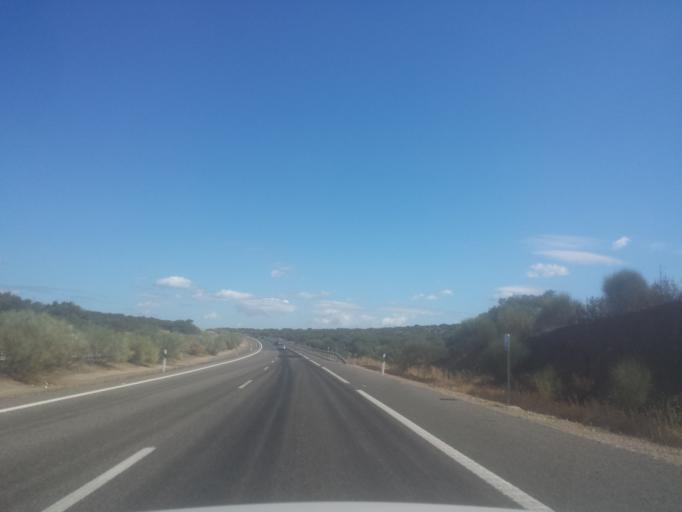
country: ES
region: Andalusia
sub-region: Provincia de Huelva
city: Santa Olalla del Cala
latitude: 37.8586
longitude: -6.2178
